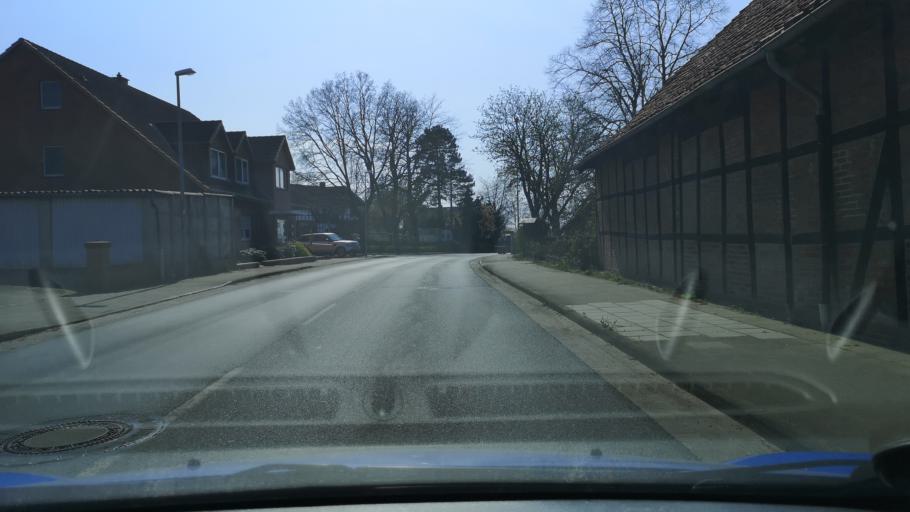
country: DE
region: Lower Saxony
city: Neustadt am Rubenberge
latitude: 52.5294
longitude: 9.4824
